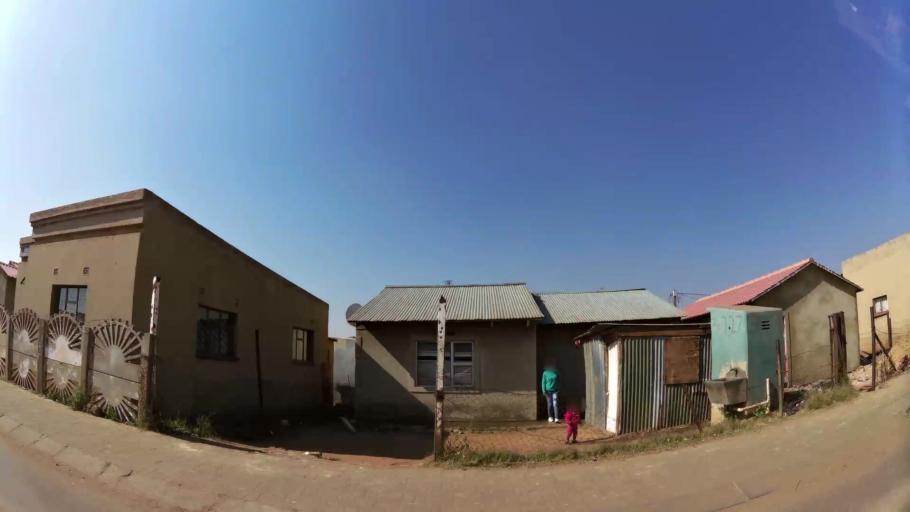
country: ZA
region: Gauteng
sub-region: Ekurhuleni Metropolitan Municipality
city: Benoni
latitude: -26.2251
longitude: 28.3095
